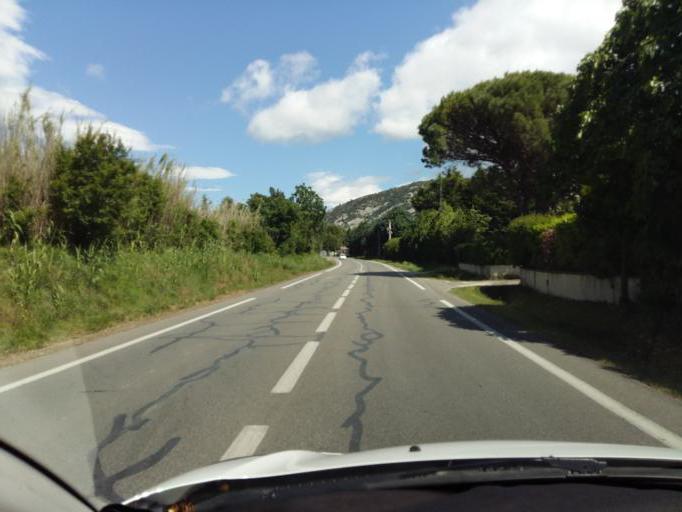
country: FR
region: Provence-Alpes-Cote d'Azur
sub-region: Departement du Vaucluse
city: Taillades
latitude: 43.8448
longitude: 5.0901
